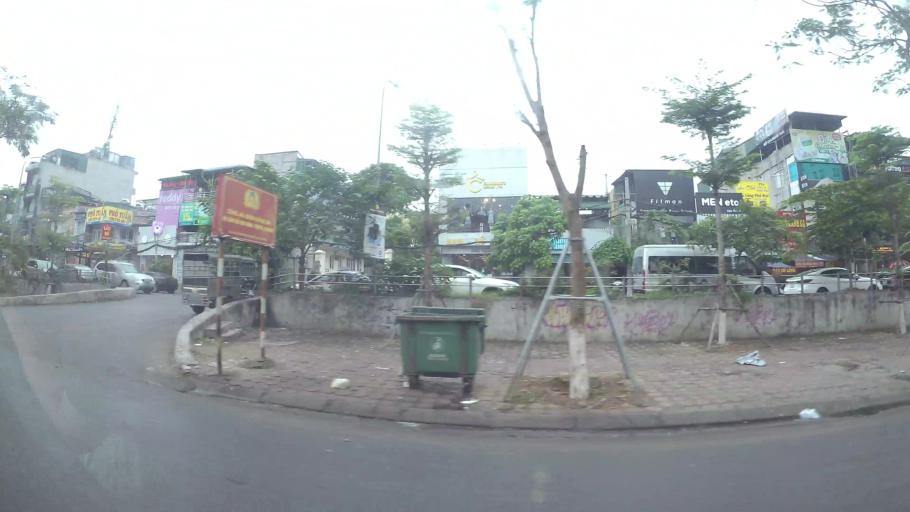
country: VN
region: Ha Noi
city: Dong Da
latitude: 21.0156
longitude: 105.8166
